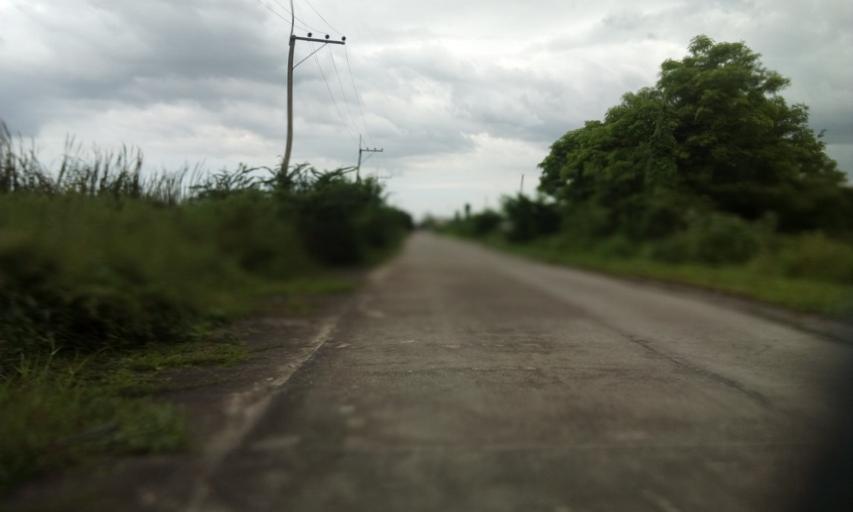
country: TH
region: Pathum Thani
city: Nong Suea
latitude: 14.0647
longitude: 100.8354
